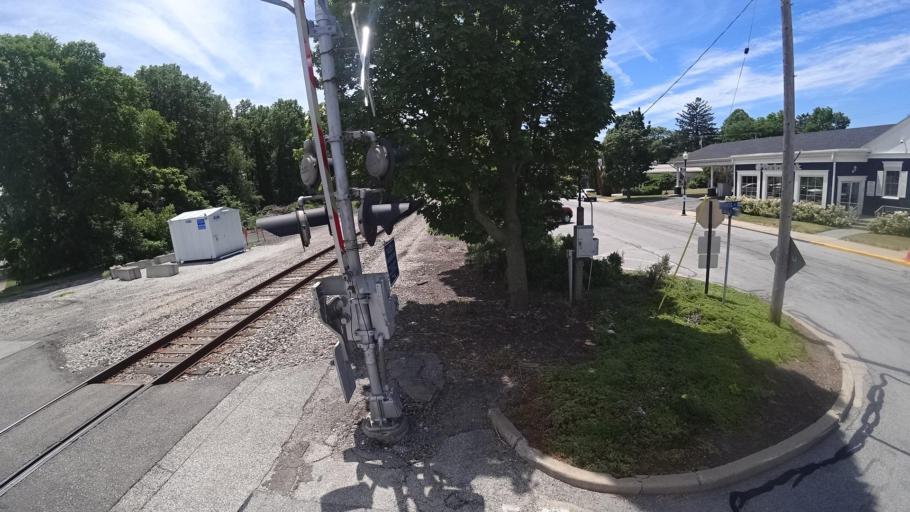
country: US
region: Indiana
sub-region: Porter County
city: Porter
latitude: 41.6156
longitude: -87.0720
